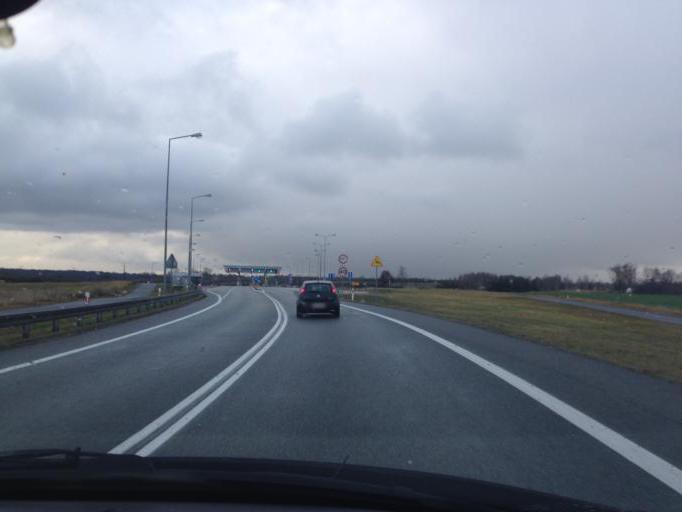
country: PL
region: Opole Voivodeship
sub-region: Powiat strzelecki
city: Ujazd
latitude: 50.4512
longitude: 18.3466
